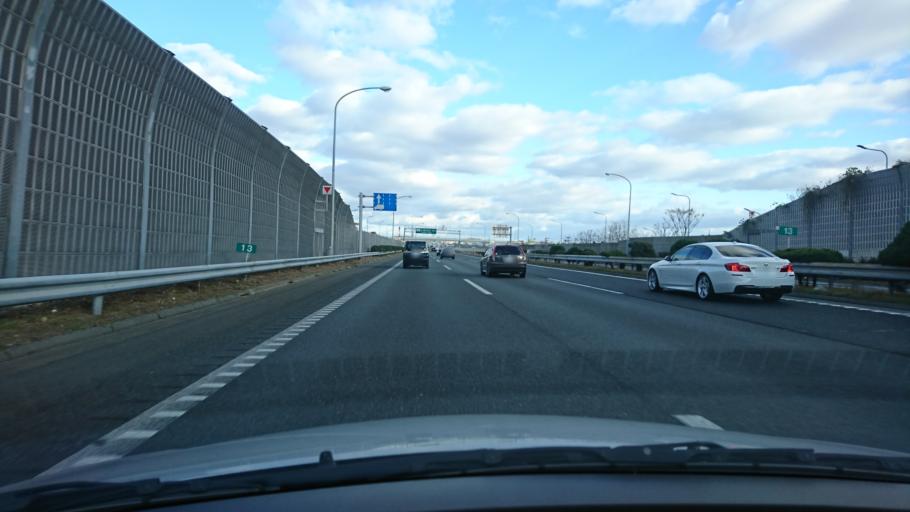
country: JP
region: Hyogo
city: Kawanishi
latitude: 34.8113
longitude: 135.4081
